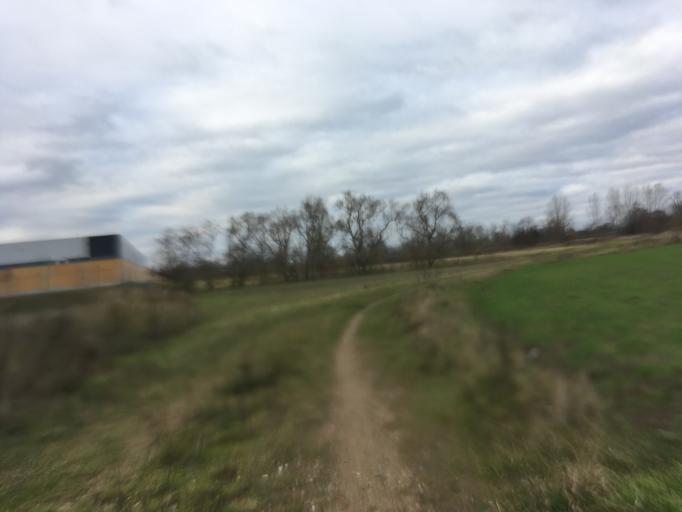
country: DE
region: Berlin
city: Bohnsdorf
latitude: 52.3929
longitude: 13.5528
